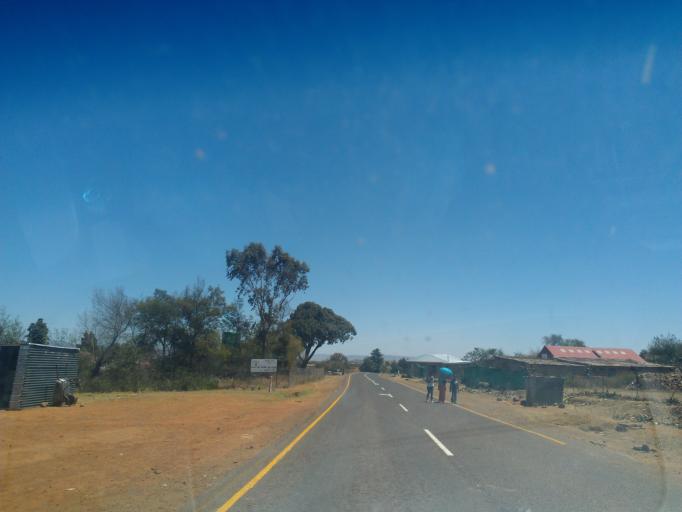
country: LS
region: Berea
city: Teyateyaneng
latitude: -29.2578
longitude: 27.7245
